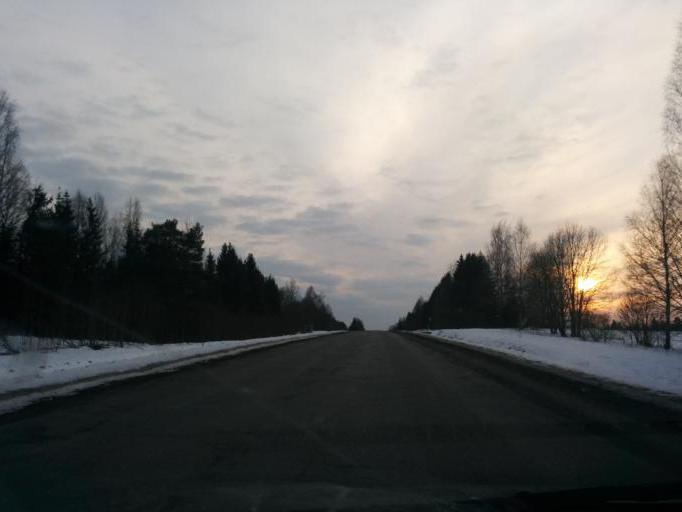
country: LV
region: Priekuli
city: Priekuli
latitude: 57.2753
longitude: 25.4795
